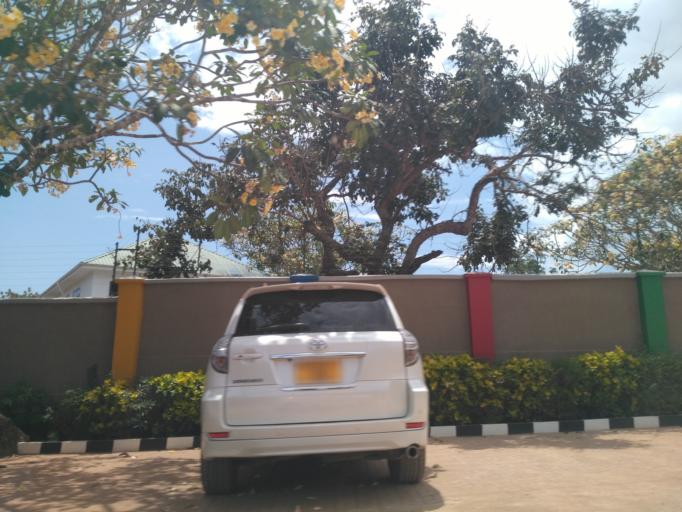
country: TZ
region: Dar es Salaam
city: Magomeni
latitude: -6.7610
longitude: 39.2729
